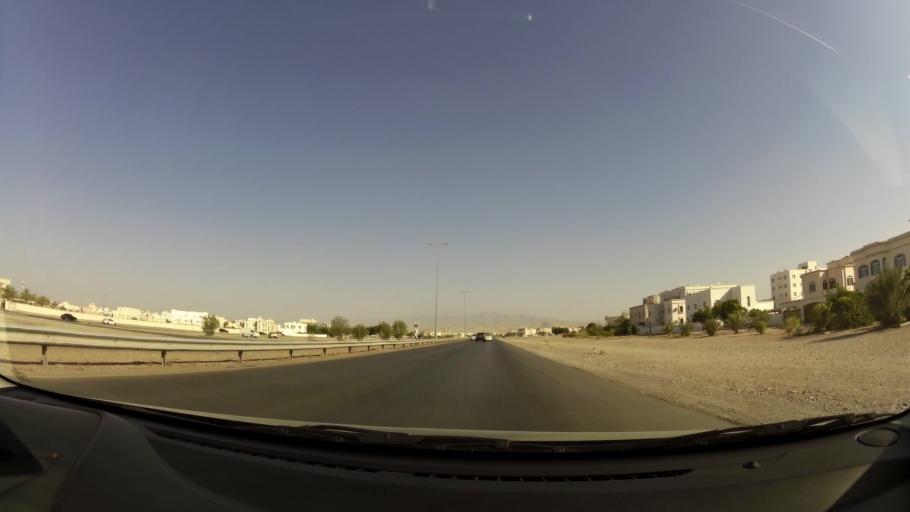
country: OM
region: Muhafazat Masqat
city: As Sib al Jadidah
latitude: 23.6183
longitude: 58.2136
